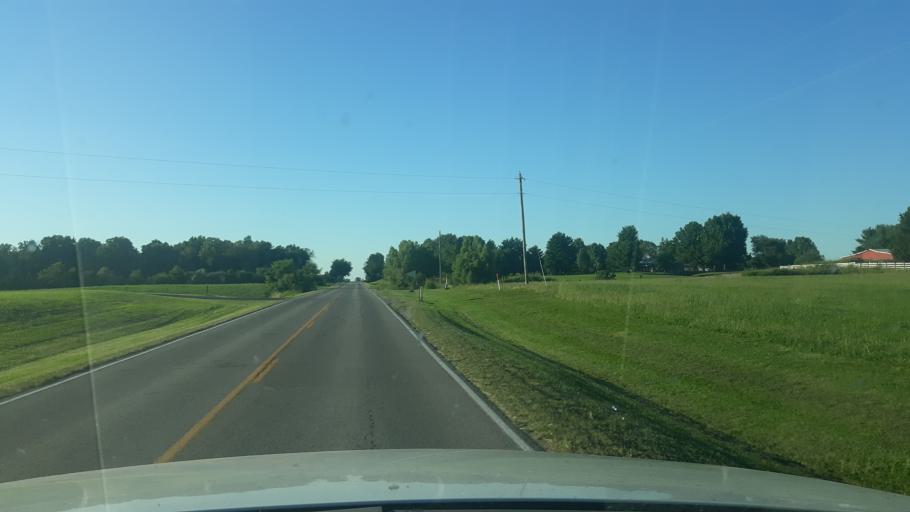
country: US
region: Illinois
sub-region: Saline County
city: Harrisburg
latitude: 37.8577
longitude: -88.6055
